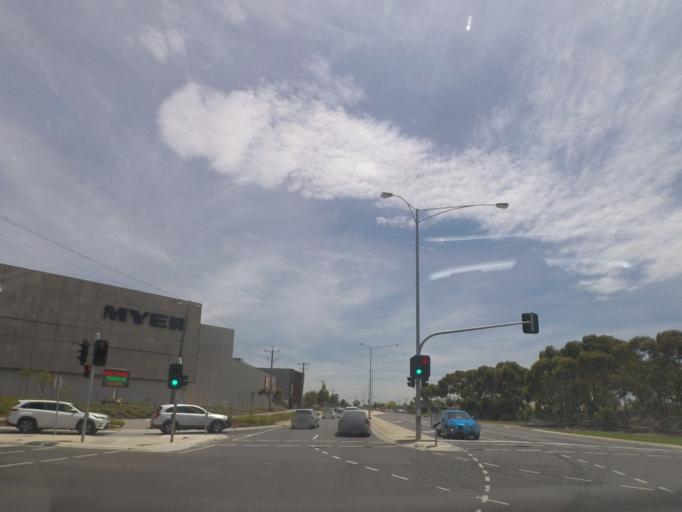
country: AU
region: Victoria
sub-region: Wyndham
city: Hoppers Crossing
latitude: -37.8775
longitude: 144.6828
